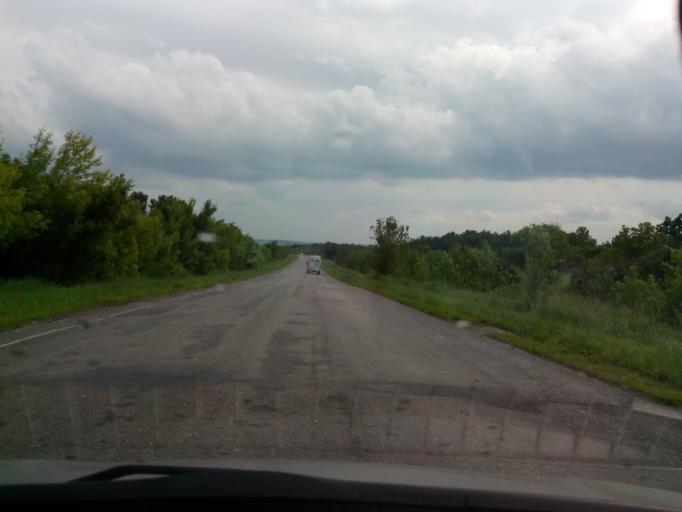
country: RU
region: Volgograd
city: Mikhaylovka
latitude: 49.9972
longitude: 43.1144
